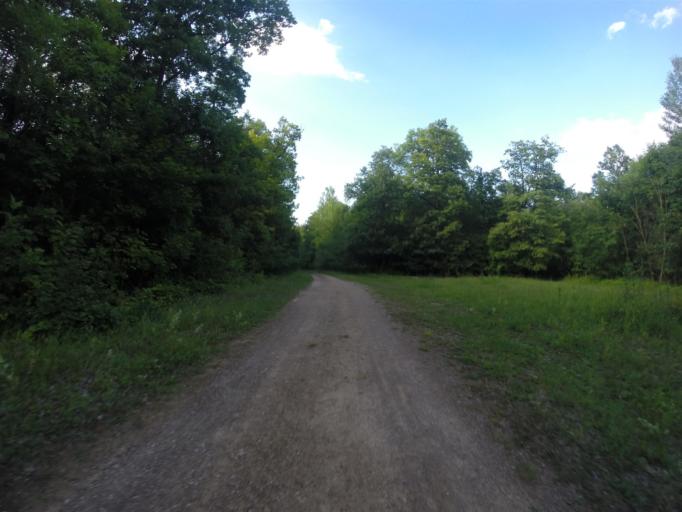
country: DE
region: Thuringia
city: Golmsdorf
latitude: 50.9489
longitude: 11.6722
